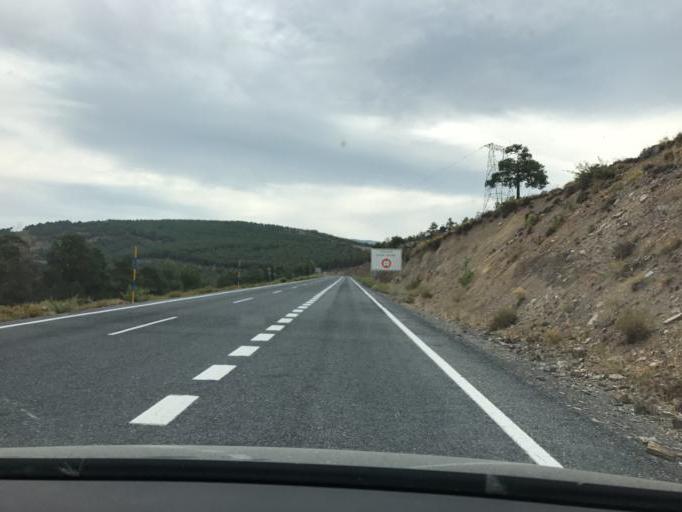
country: ES
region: Andalusia
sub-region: Provincia de Granada
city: Aldeire
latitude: 37.1423
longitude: -3.0479
